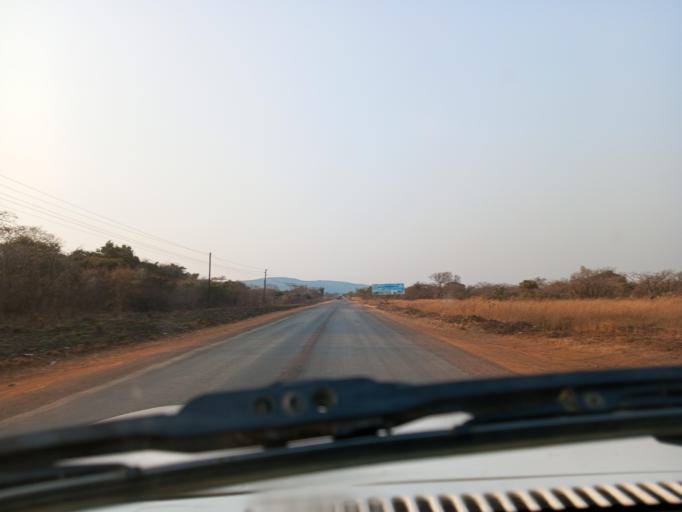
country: ZM
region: Northern
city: Mpika
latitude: -11.9196
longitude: 31.4166
